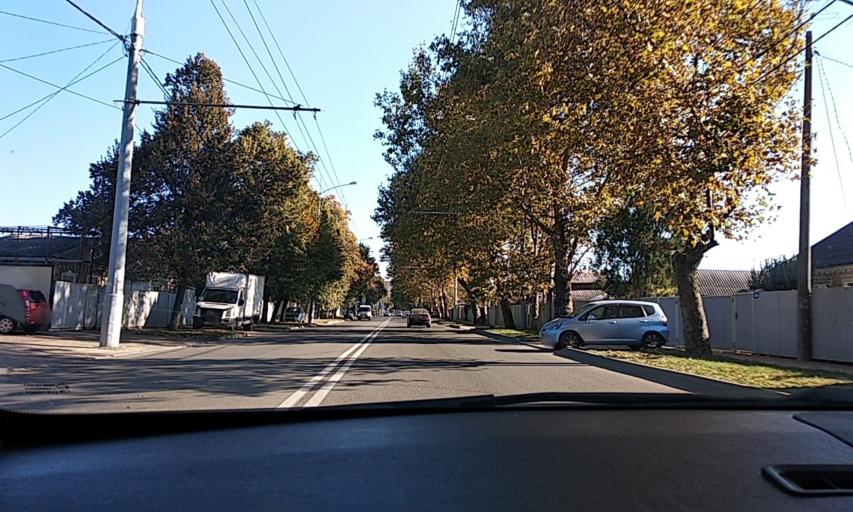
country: RU
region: Krasnodarskiy
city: Pashkovskiy
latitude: 45.0257
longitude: 39.1157
